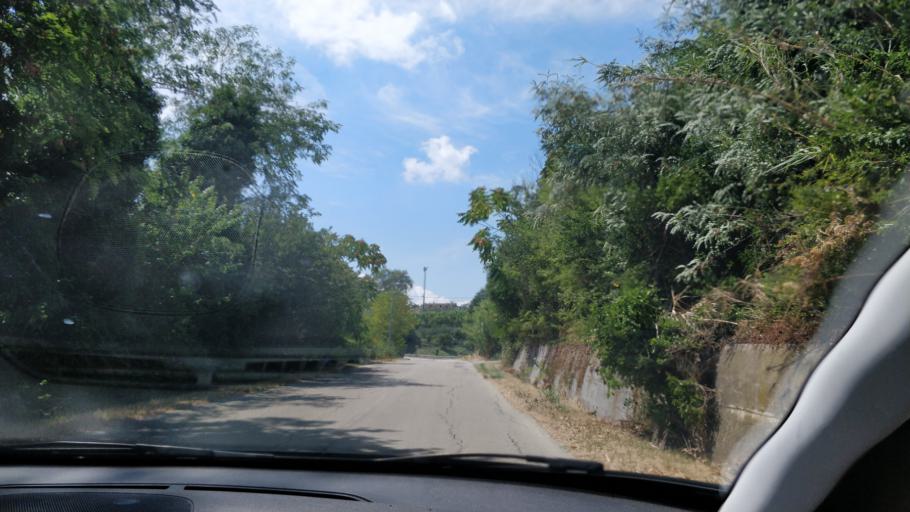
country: IT
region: Abruzzo
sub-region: Provincia di Chieti
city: Sambuceto
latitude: 42.4118
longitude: 14.2069
